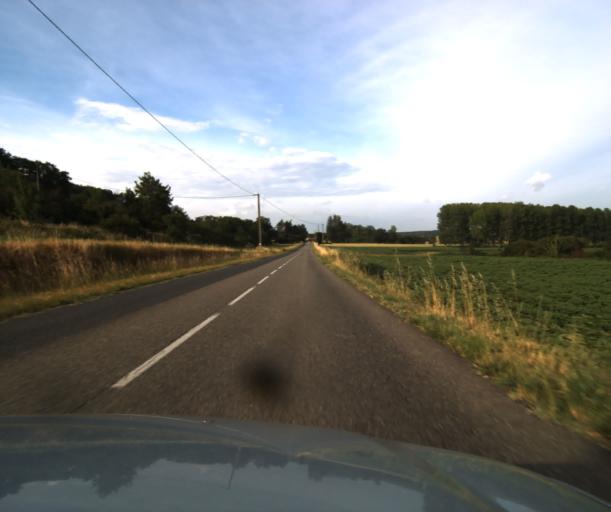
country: FR
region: Midi-Pyrenees
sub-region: Departement du Tarn-et-Garonne
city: Castelsarrasin
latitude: 43.9653
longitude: 1.1092
